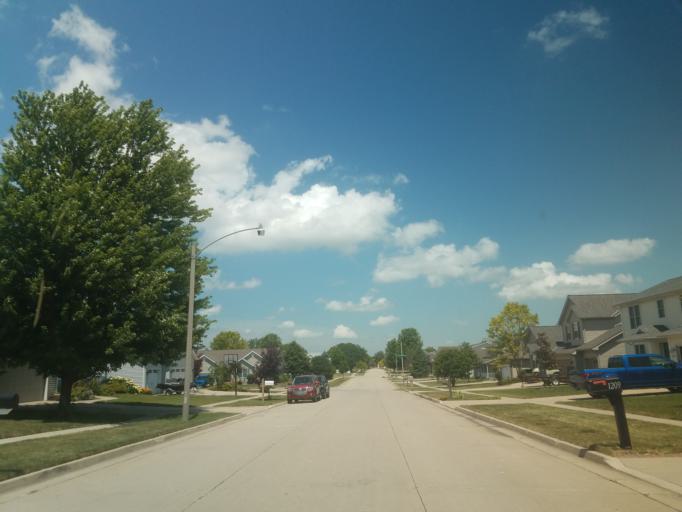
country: US
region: Illinois
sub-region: McLean County
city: Normal
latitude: 40.4961
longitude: -88.9192
